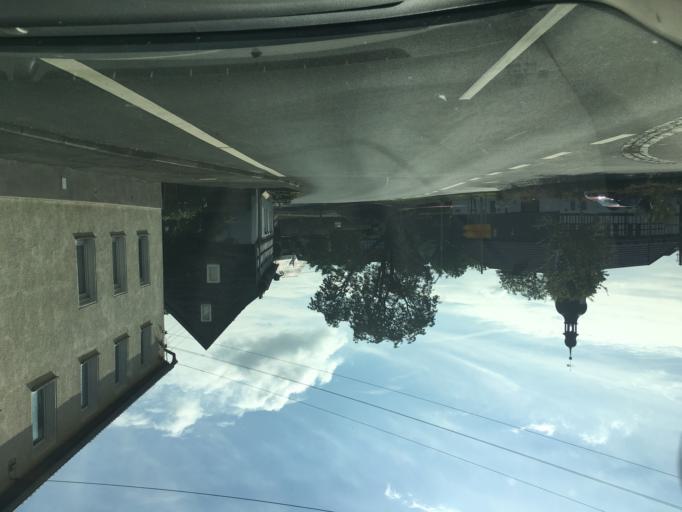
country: DE
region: Thuringia
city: Mittelpollnitz
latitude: 50.7351
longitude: 11.9120
